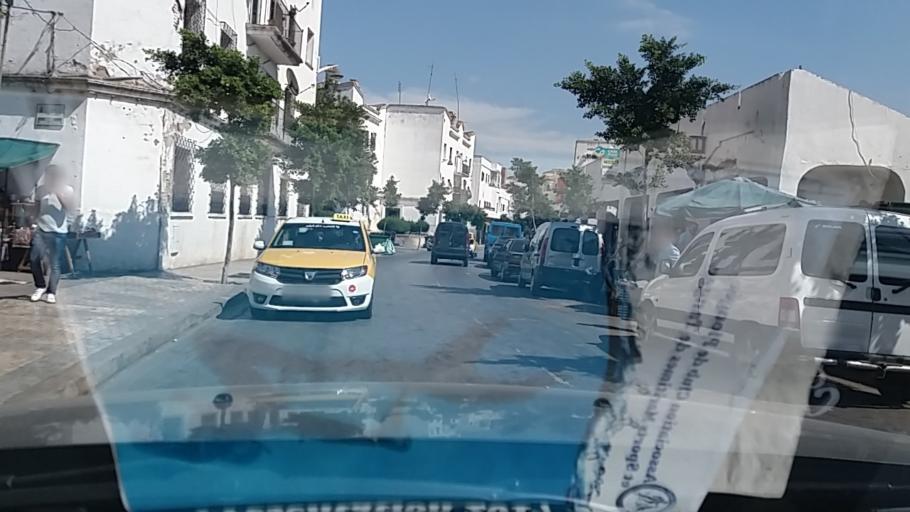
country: MA
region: Tanger-Tetouan
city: Tetouan
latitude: 35.5744
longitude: -5.3844
